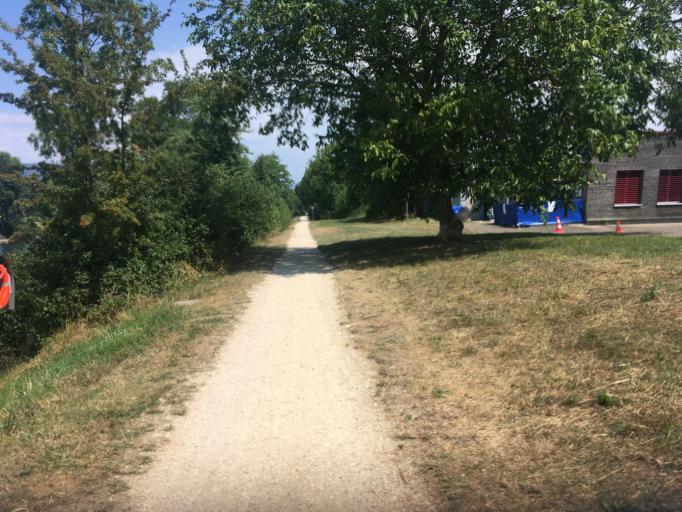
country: CH
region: Bern
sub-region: Biel/Bienne District
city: Orpund
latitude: 47.1289
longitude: 7.3008
